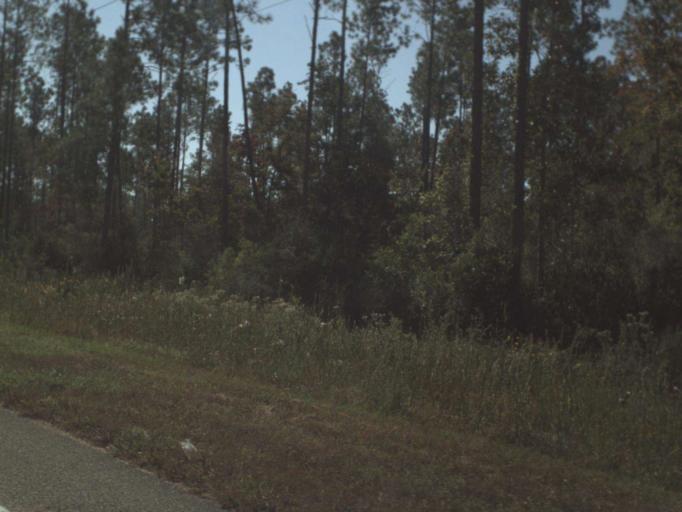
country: US
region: Florida
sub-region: Leon County
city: Woodville
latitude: 30.2121
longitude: -84.1959
